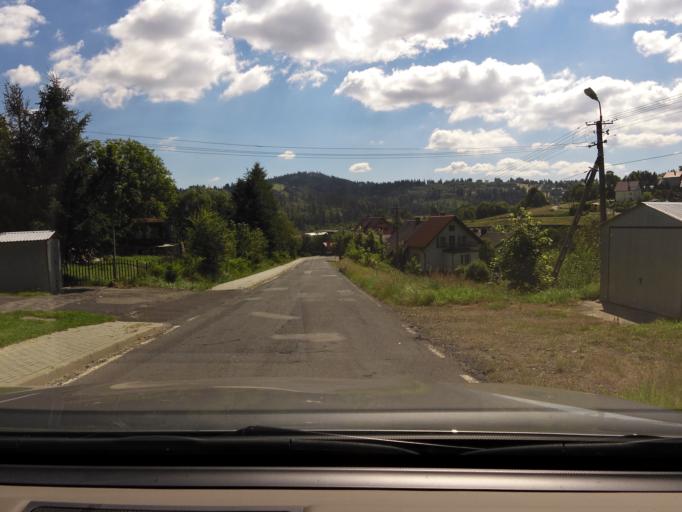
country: PL
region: Silesian Voivodeship
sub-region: Powiat cieszynski
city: Koniakow
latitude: 49.5124
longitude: 18.9681
